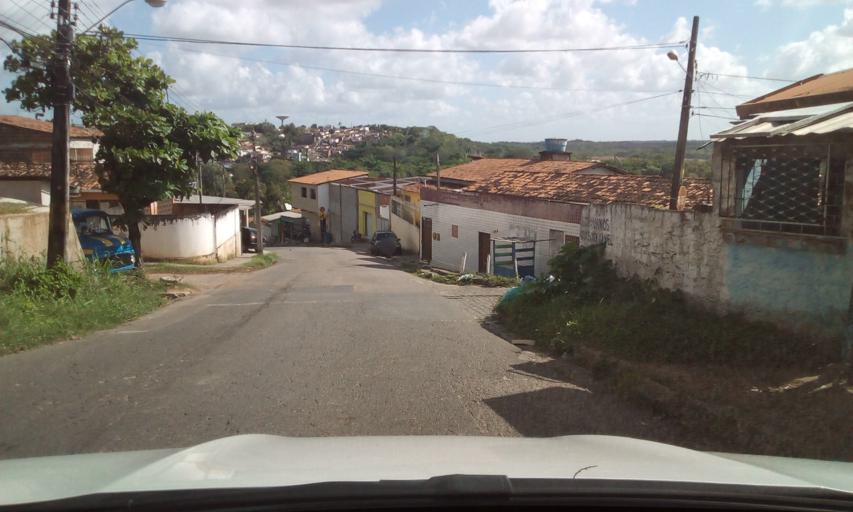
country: BR
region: Paraiba
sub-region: Joao Pessoa
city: Joao Pessoa
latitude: -7.1282
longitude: -34.8861
